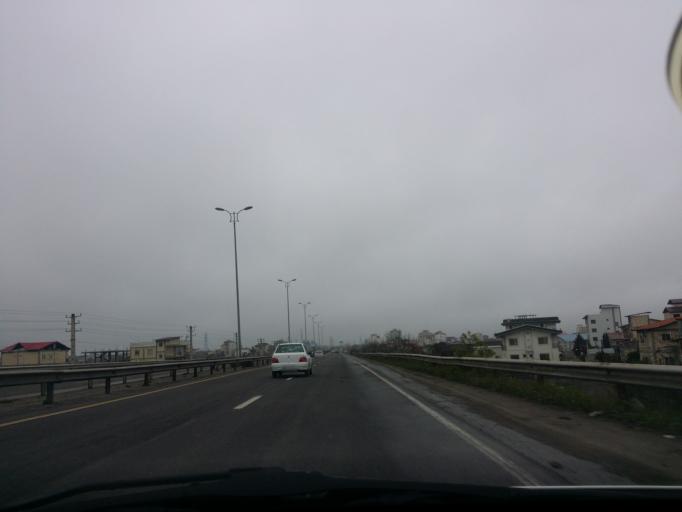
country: IR
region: Mazandaran
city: Tonekabon
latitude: 36.8066
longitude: 50.8708
